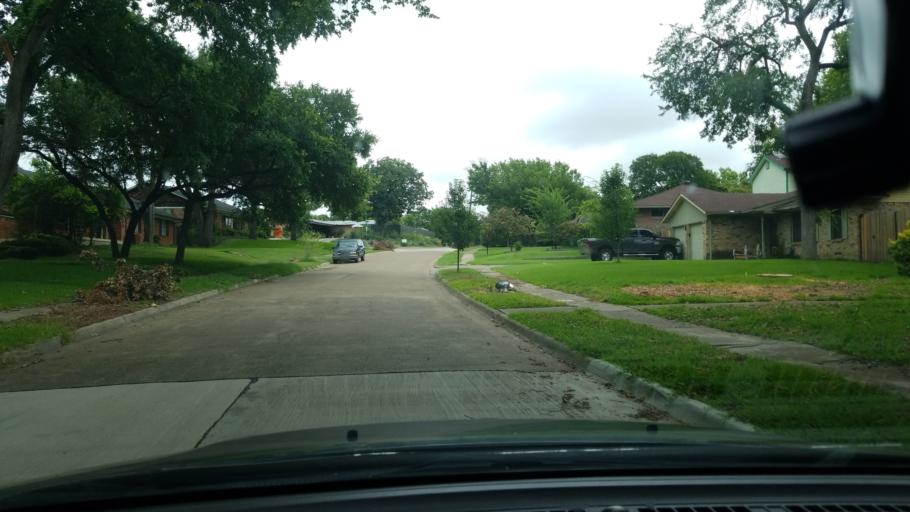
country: US
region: Texas
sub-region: Dallas County
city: Highland Park
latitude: 32.8102
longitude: -96.6974
